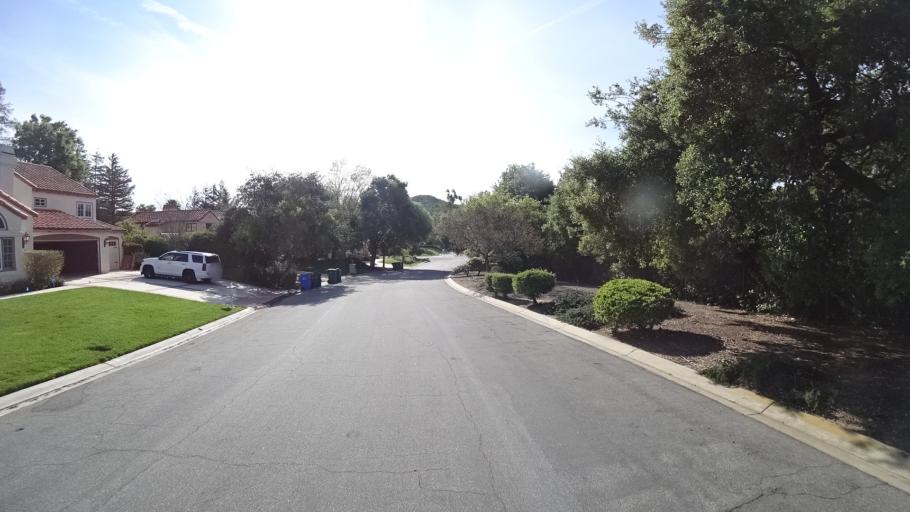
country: US
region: California
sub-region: Ventura County
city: Oak Park
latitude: 34.1938
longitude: -118.7927
